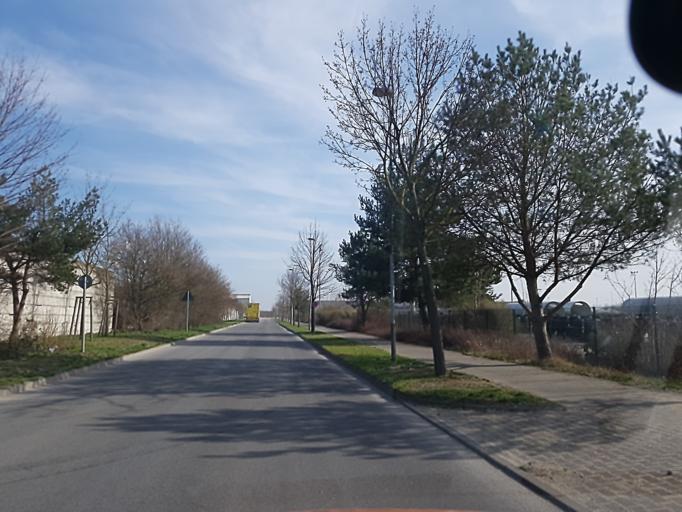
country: DE
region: Brandenburg
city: Finsterwalde
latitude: 51.6349
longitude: 13.7455
